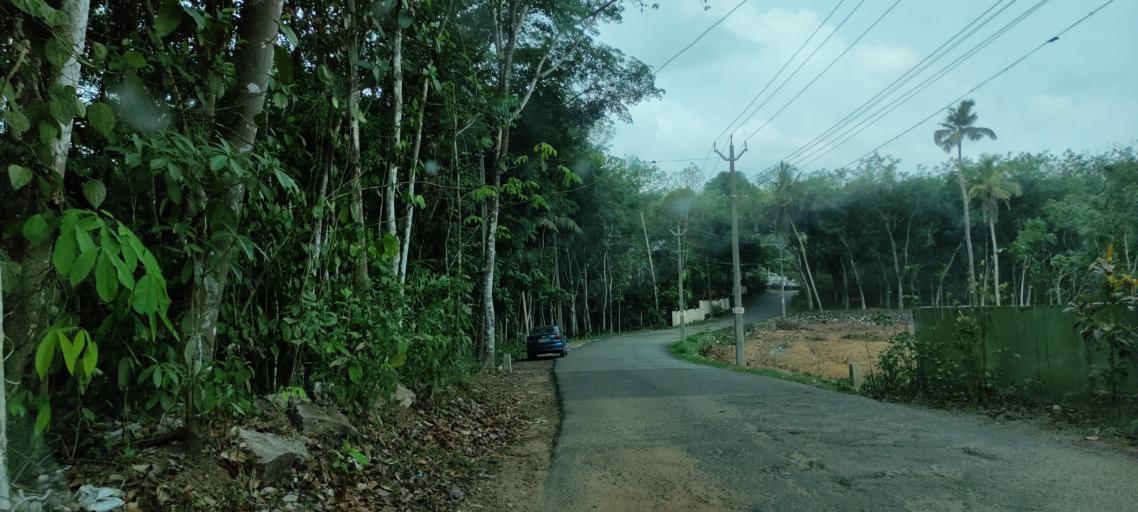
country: IN
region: Kerala
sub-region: Pattanamtitta
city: Adur
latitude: 9.1751
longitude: 76.7378
